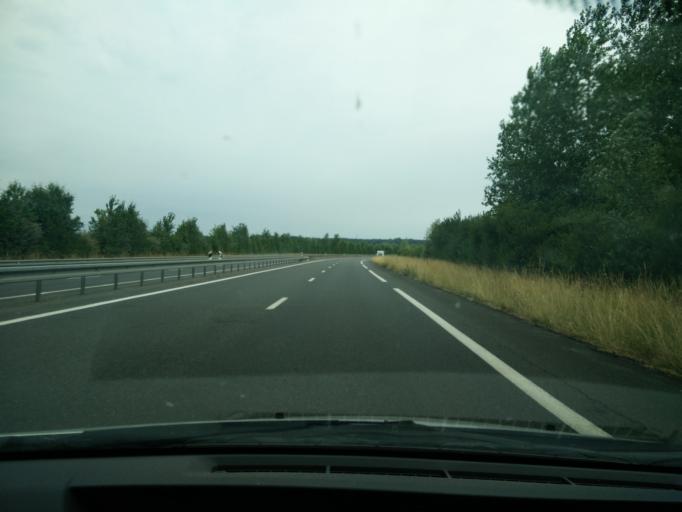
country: FR
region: Pays de la Loire
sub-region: Departement de Maine-et-Loire
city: Doue-la-Fontaine
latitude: 47.2049
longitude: -0.3135
